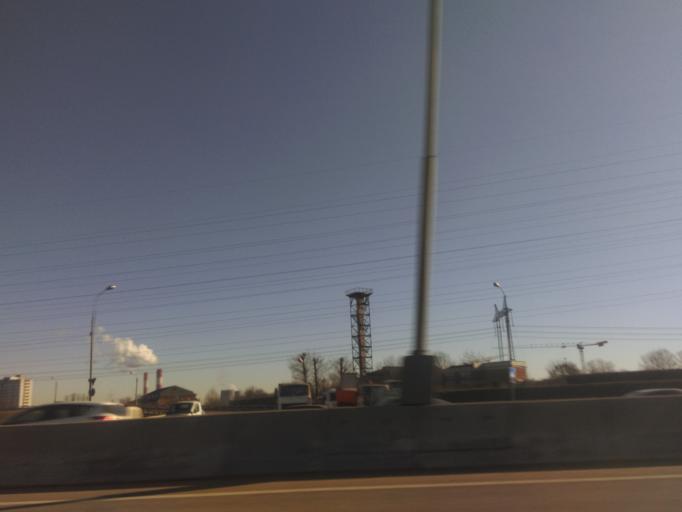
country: RU
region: Moscow
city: Mikhalkovo
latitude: 55.6814
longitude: 37.4177
